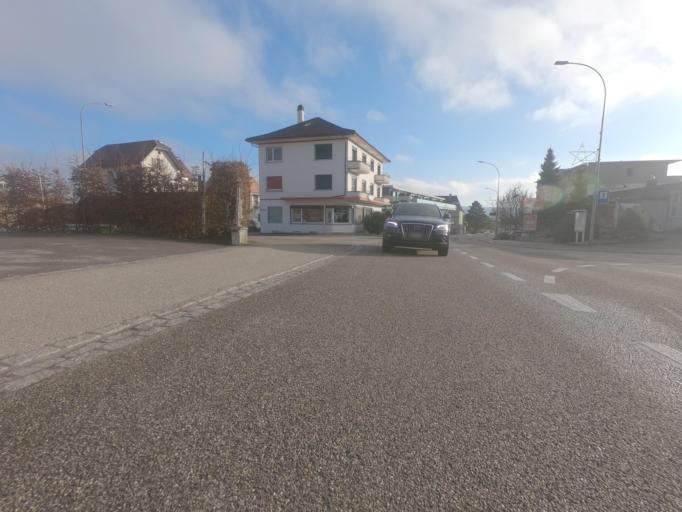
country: CH
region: Solothurn
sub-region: Bezirk Lebern
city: Bettlach
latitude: 47.2002
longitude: 7.4257
